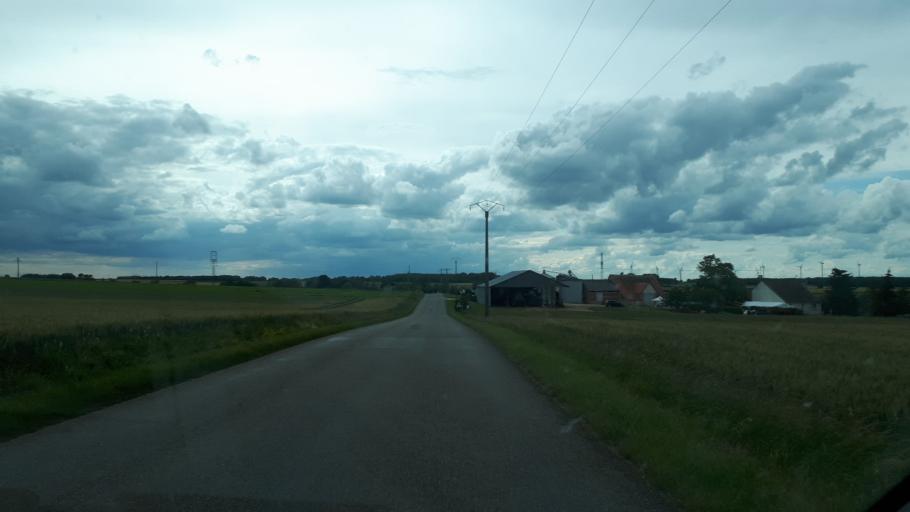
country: FR
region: Centre
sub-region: Departement de l'Indre
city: Reuilly
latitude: 47.0942
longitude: 2.0039
